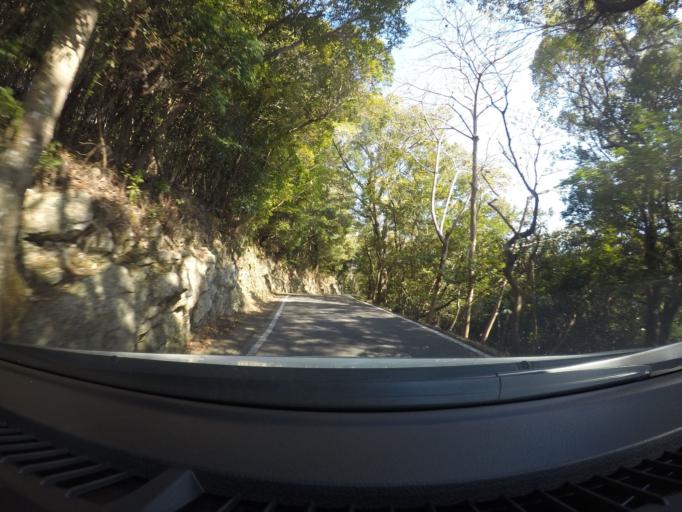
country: JP
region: Kochi
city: Kochi-shi
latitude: 33.5464
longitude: 133.5733
